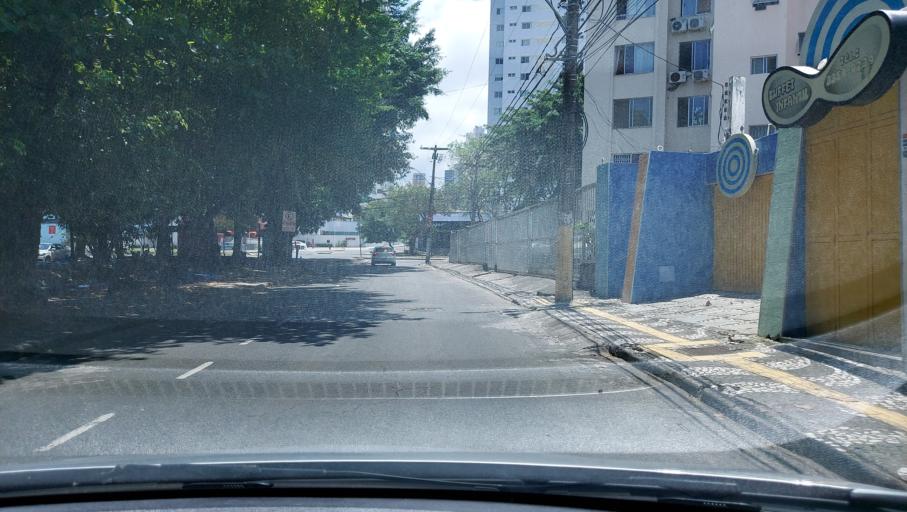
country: BR
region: Bahia
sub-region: Salvador
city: Salvador
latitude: -12.9911
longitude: -38.4535
